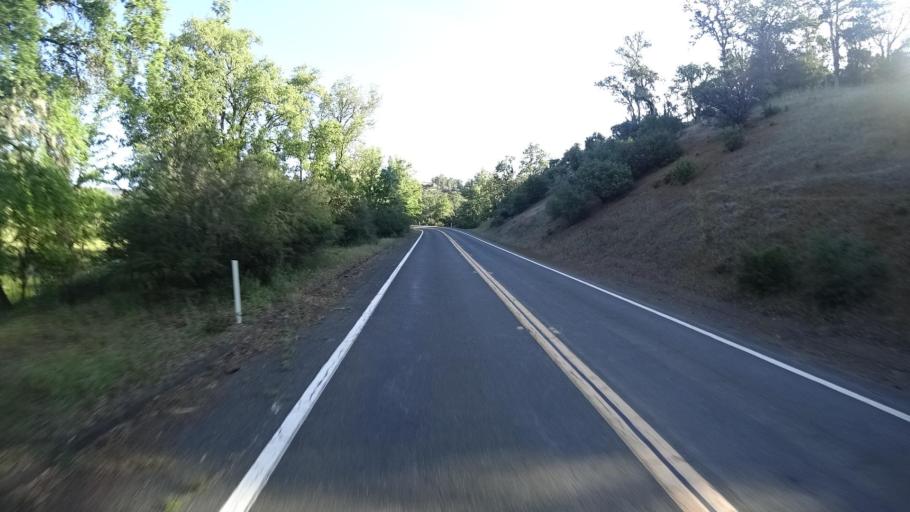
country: US
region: California
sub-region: Lake County
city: North Lakeport
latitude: 39.1010
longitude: -122.9686
